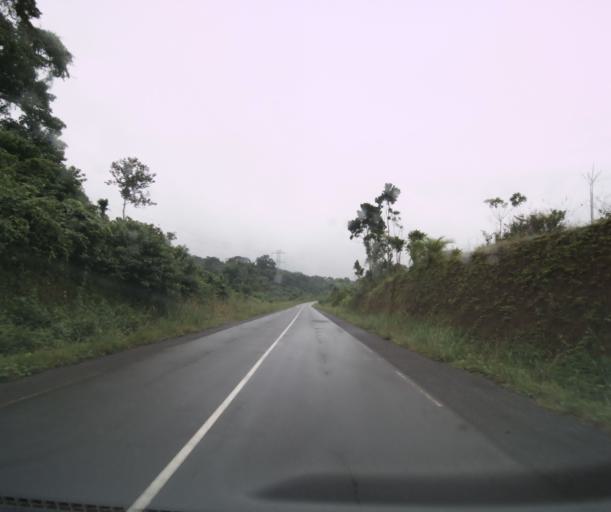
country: CM
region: Littoral
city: Dizangue
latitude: 3.3644
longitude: 10.1027
